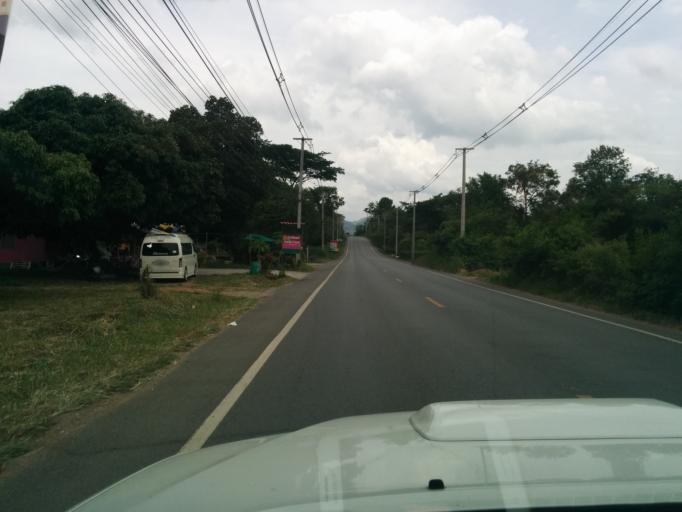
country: TH
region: Sara Buri
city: Muak Lek
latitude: 14.6139
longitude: 101.2123
